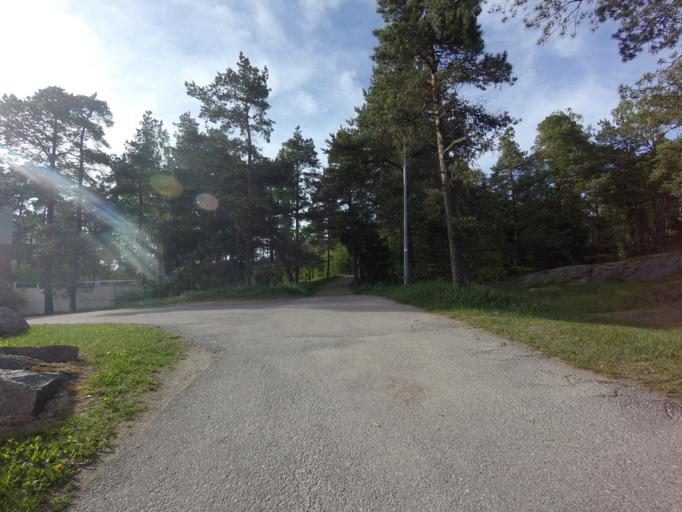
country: FI
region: Uusimaa
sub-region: Helsinki
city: Koukkuniemi
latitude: 60.1563
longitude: 24.7316
